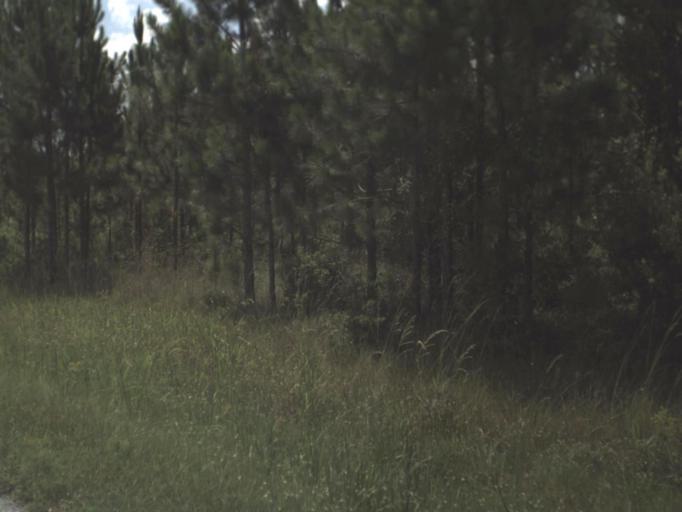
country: US
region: Florida
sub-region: Baker County
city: Macclenny
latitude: 30.5128
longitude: -82.2499
